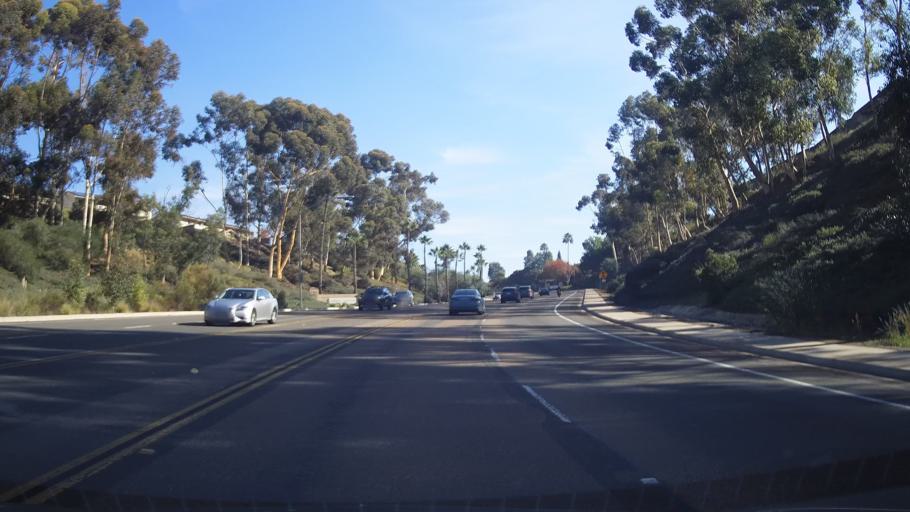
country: US
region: California
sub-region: San Diego County
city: La Mesa
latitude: 32.8109
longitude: -117.1095
